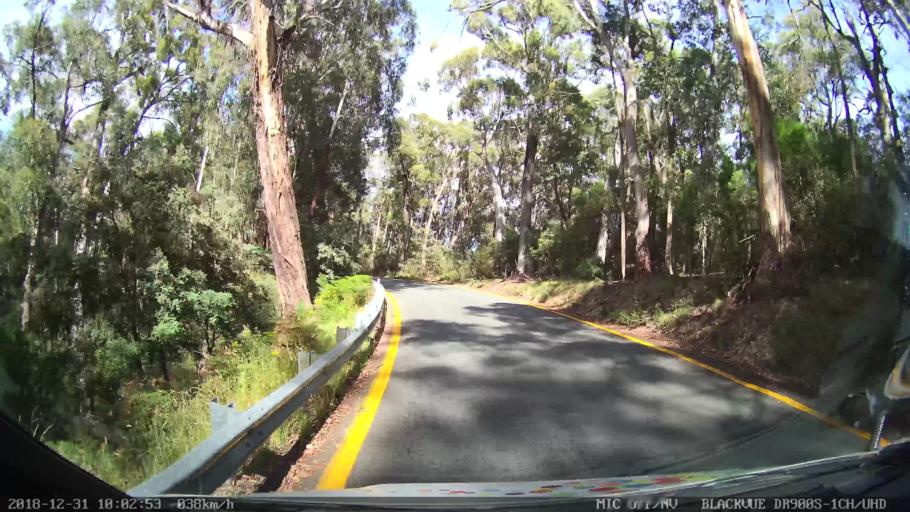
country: AU
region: New South Wales
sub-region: Snowy River
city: Jindabyne
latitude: -36.5304
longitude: 148.1952
